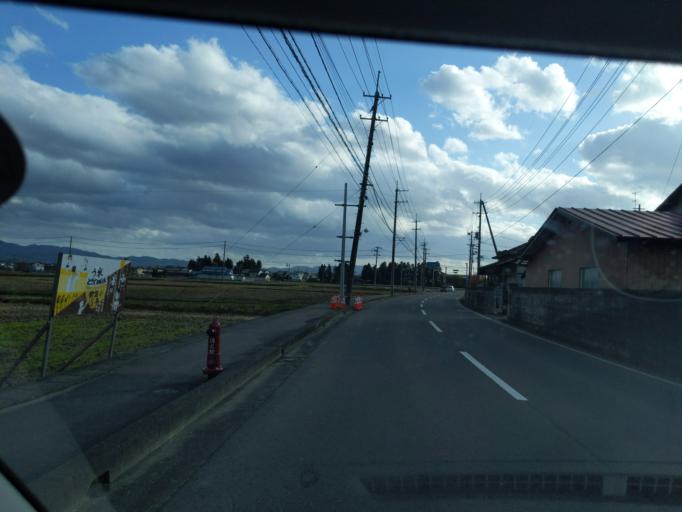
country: JP
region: Iwate
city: Mizusawa
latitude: 39.1448
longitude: 141.1589
